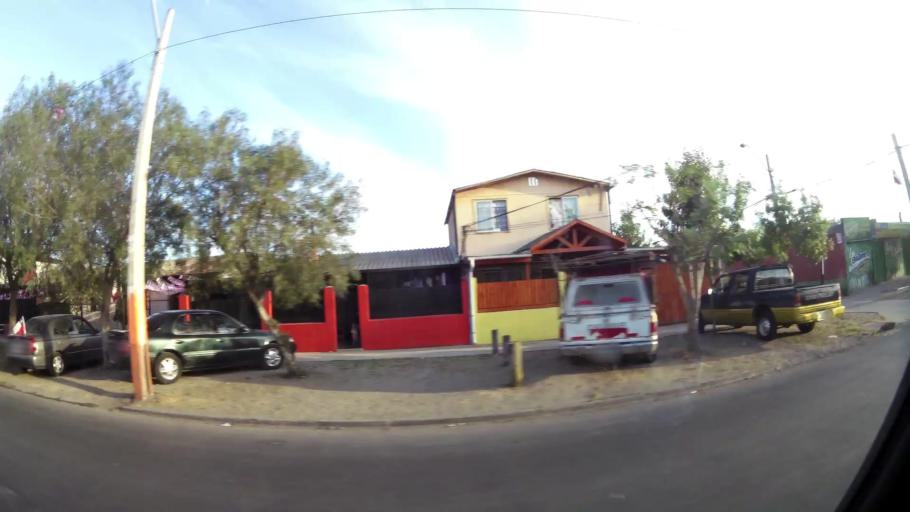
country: CL
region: Santiago Metropolitan
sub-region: Provincia de Santiago
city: Lo Prado
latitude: -33.4517
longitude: -70.7205
